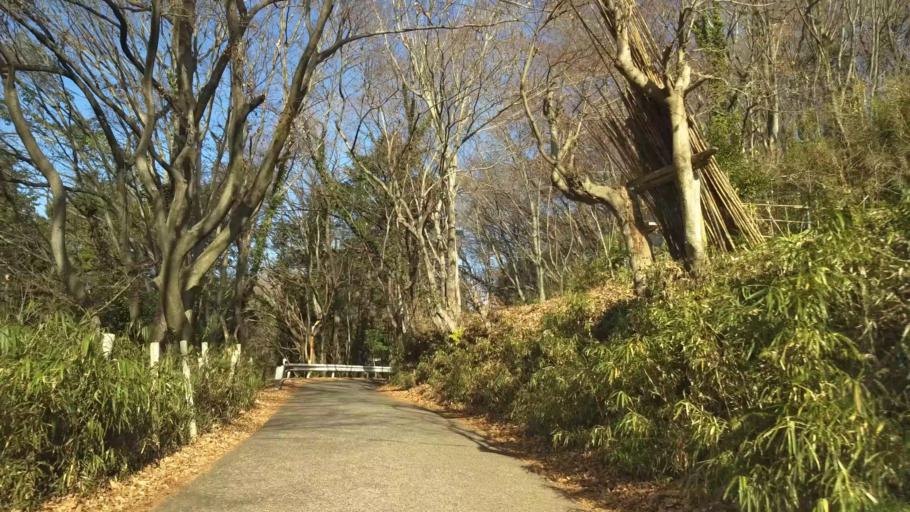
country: JP
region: Kanagawa
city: Hadano
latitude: 35.3737
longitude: 139.2400
